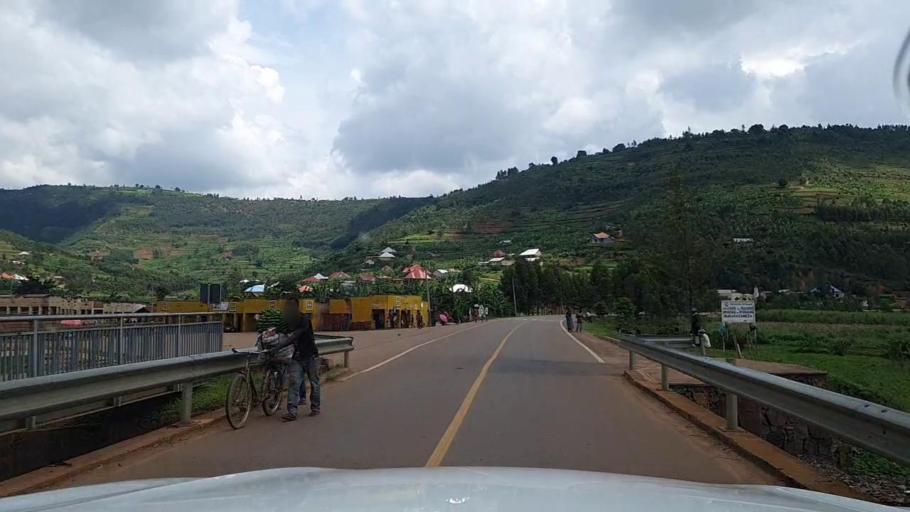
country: RW
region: Kigali
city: Kigali
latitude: -1.8134
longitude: 30.0967
